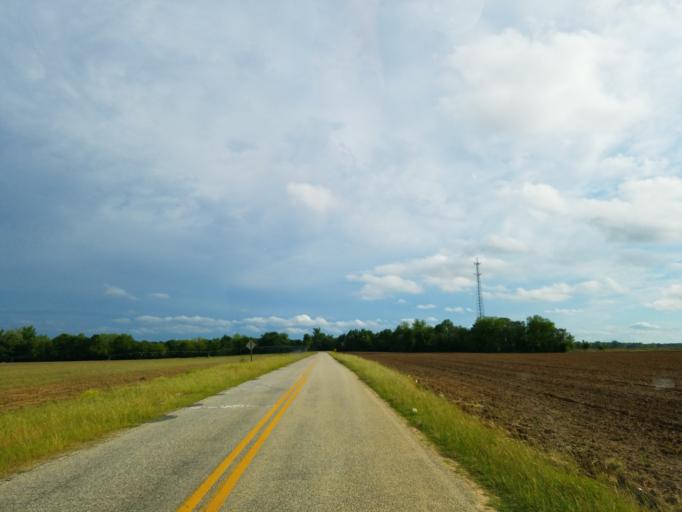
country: US
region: Georgia
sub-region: Dooly County
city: Vienna
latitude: 32.1721
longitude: -83.7655
